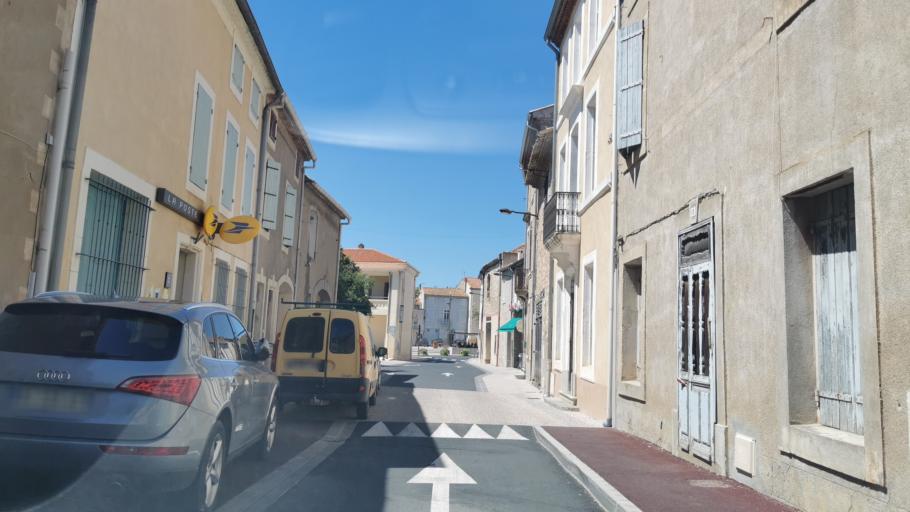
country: FR
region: Languedoc-Roussillon
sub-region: Departement de l'Aude
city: Fleury
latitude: 43.2281
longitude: 3.1361
